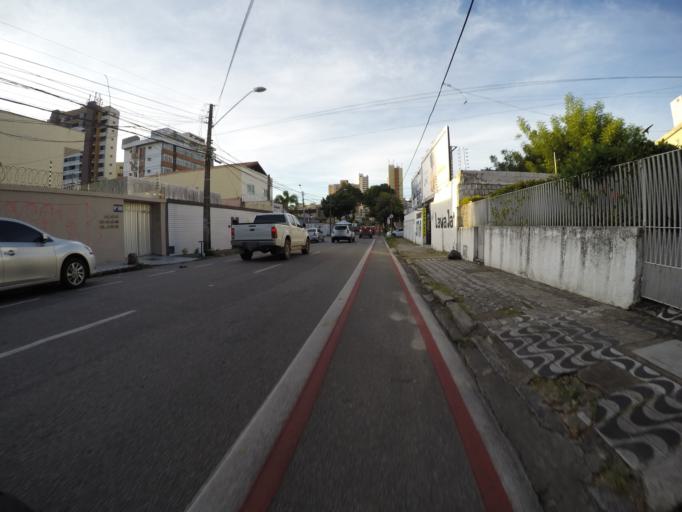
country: BR
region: Ceara
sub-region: Fortaleza
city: Fortaleza
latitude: -3.7367
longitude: -38.5119
